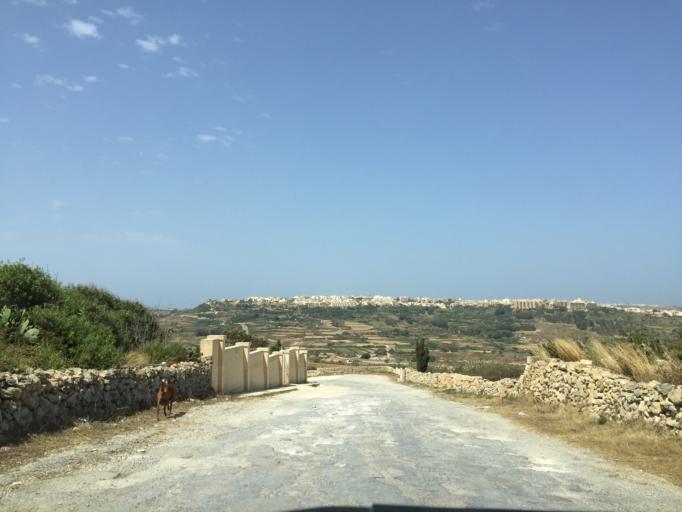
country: MT
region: In-Nadur
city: Nadur
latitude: 36.0537
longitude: 14.2921
